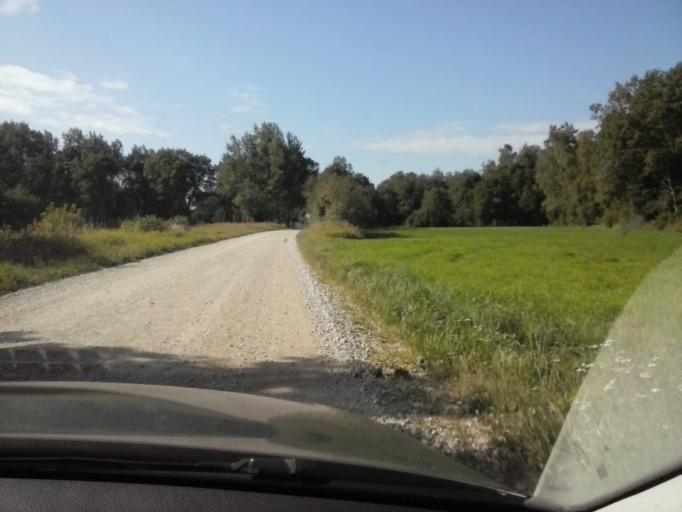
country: EE
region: Laeaene
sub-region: Haapsalu linn
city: Haapsalu
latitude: 58.8756
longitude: 23.5567
